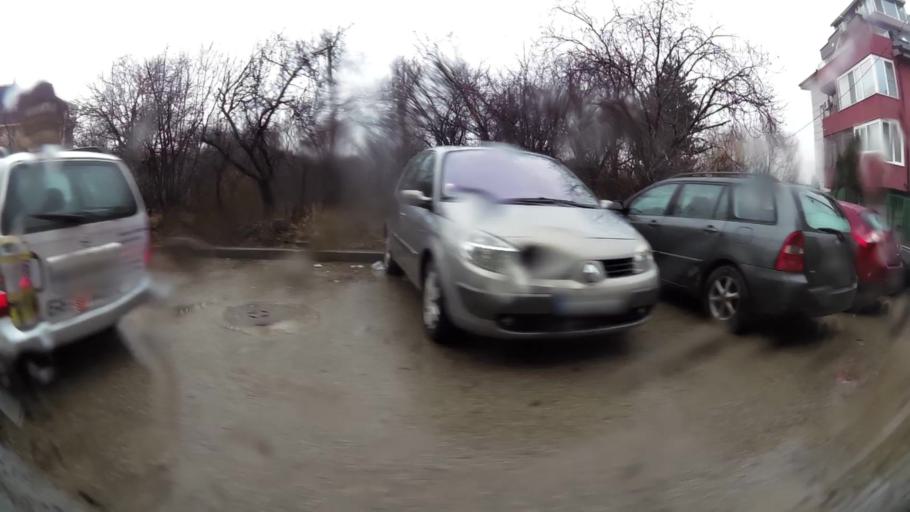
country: BG
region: Sofia-Capital
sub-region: Stolichna Obshtina
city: Sofia
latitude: 42.6515
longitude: 23.3303
